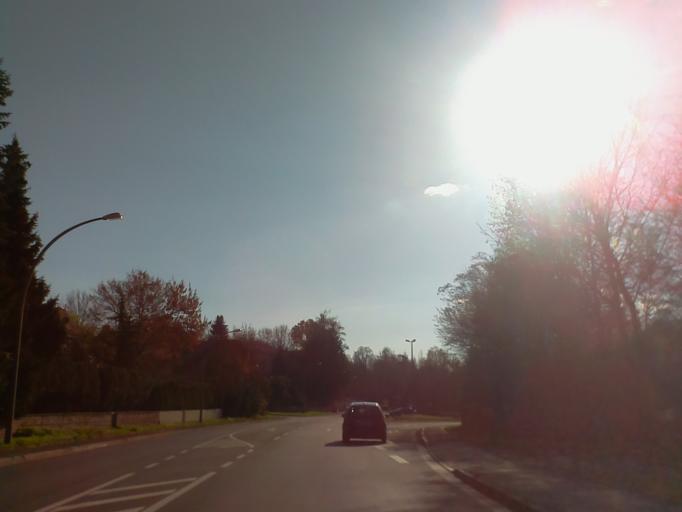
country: DE
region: Bavaria
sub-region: Regierungsbezirk Unterfranken
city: Bad Kissingen
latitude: 50.2168
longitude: 10.0723
